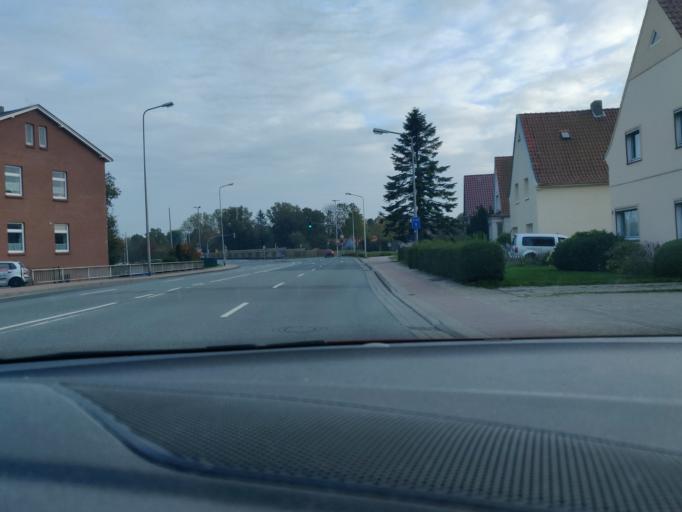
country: DE
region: Lower Saxony
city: Cuxhaven
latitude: 53.8462
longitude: 8.7291
